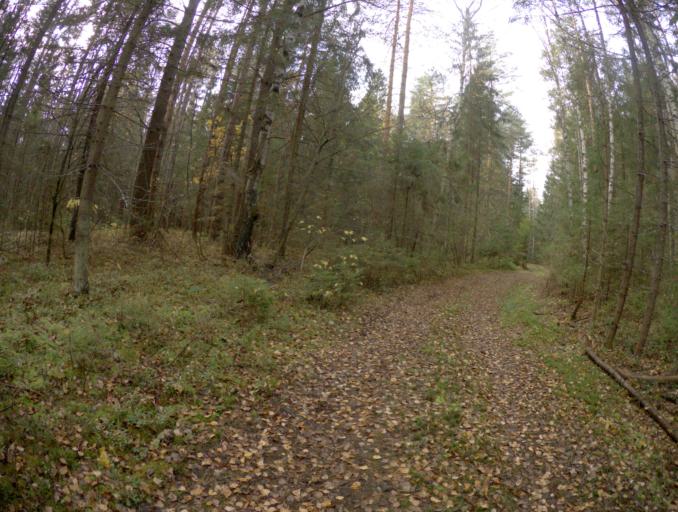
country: RU
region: Vladimir
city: Raduzhnyy
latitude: 55.9596
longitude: 40.3530
